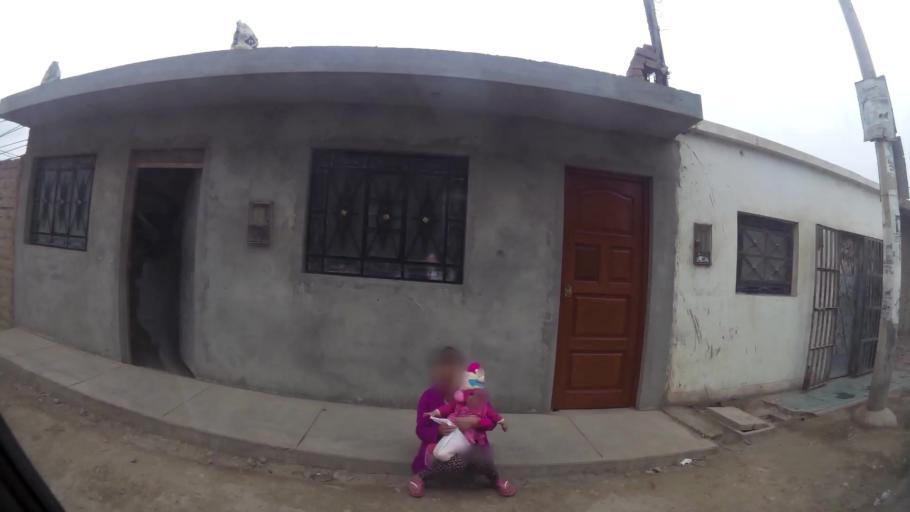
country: PE
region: Lima
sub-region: Provincia de Huaral
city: Huaral
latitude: -11.5003
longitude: -77.2348
